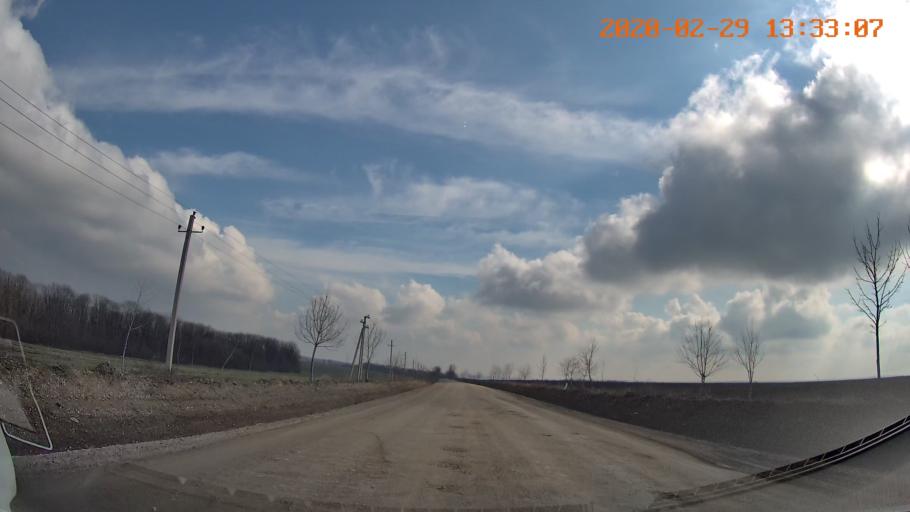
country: MD
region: Telenesti
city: Camenca
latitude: 47.8753
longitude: 28.6142
